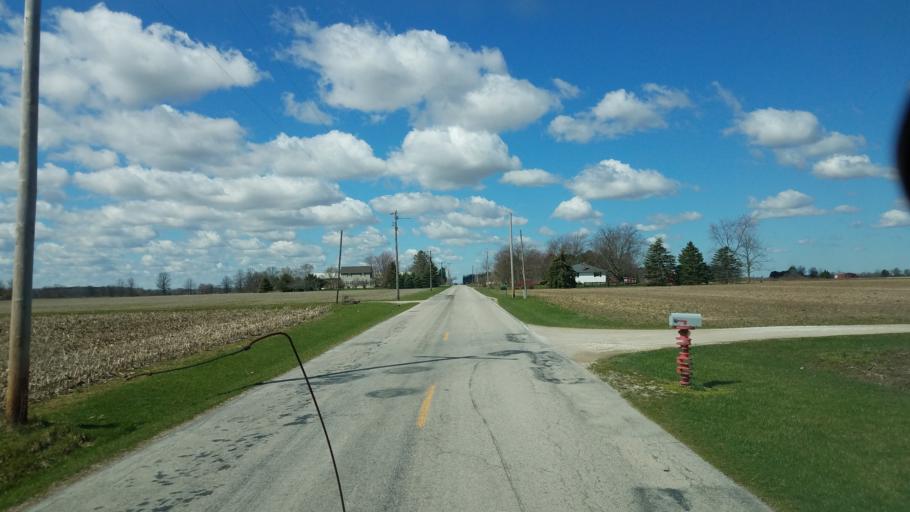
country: US
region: Ohio
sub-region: Sandusky County
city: Mount Carmel
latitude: 41.2416
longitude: -82.9632
